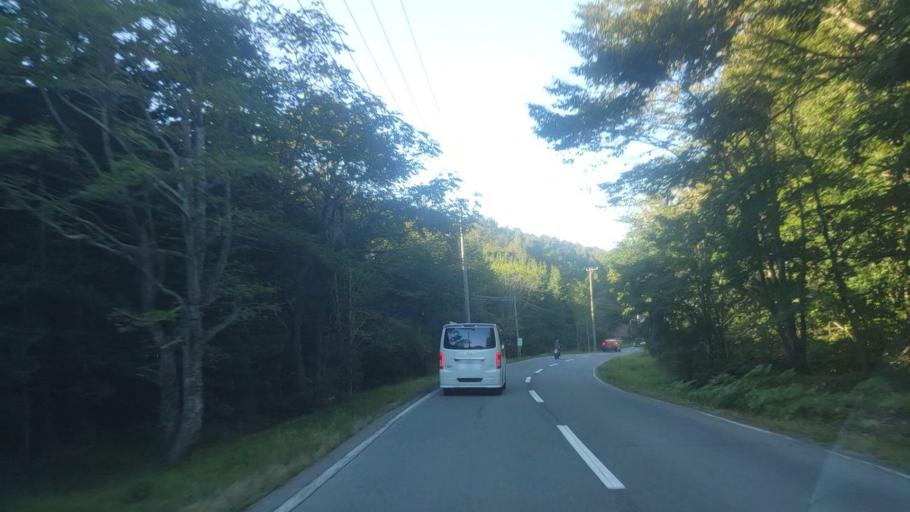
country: JP
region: Nagano
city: Kamimaruko
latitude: 36.2164
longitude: 138.2931
